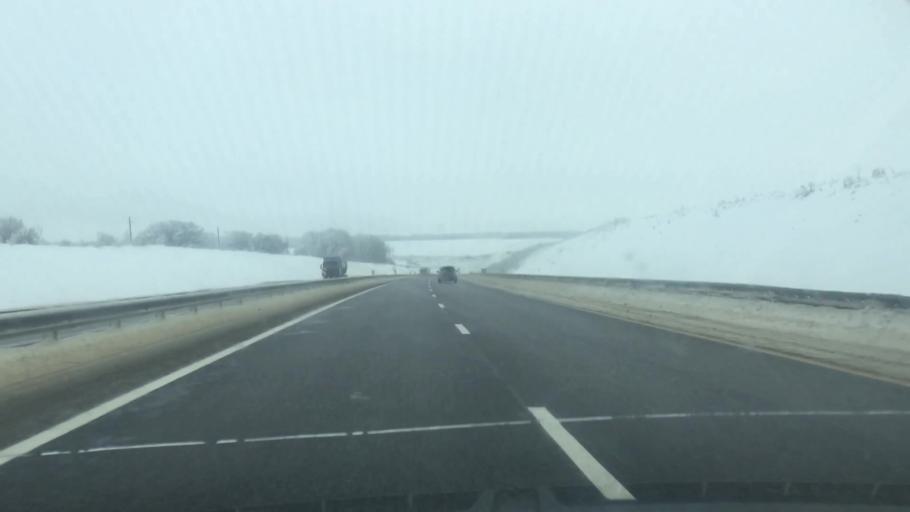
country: RU
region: Lipetsk
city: Stanovoye
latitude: 52.8732
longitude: 38.2780
